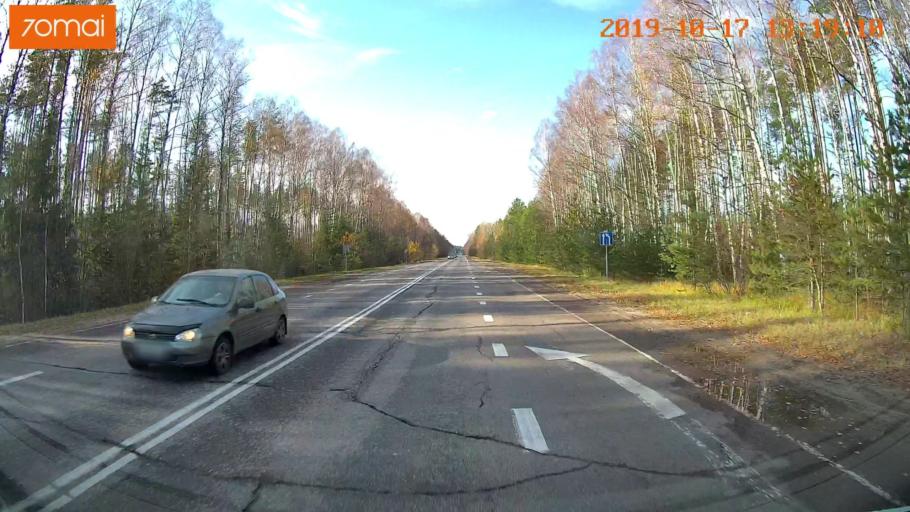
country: RU
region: Rjazan
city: Gus'-Zheleznyy
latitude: 55.0677
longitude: 41.0805
